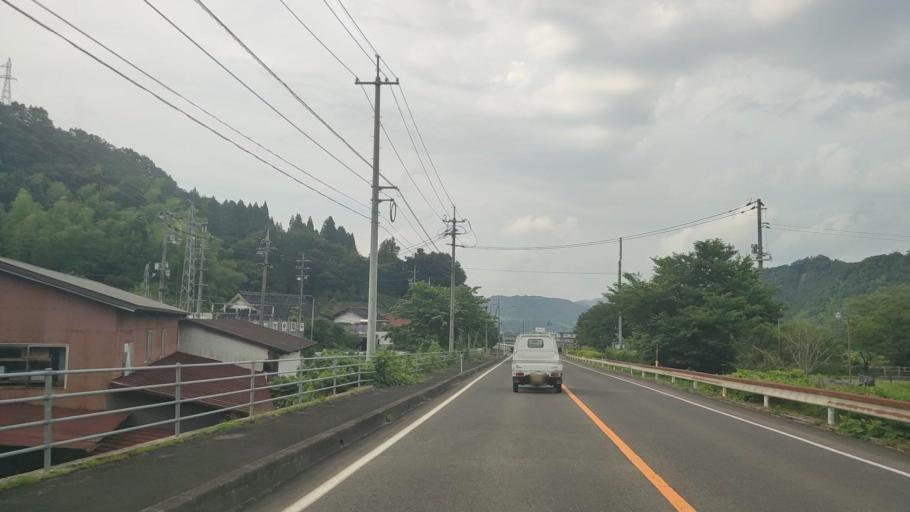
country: JP
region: Tottori
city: Kurayoshi
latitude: 35.3882
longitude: 133.8567
